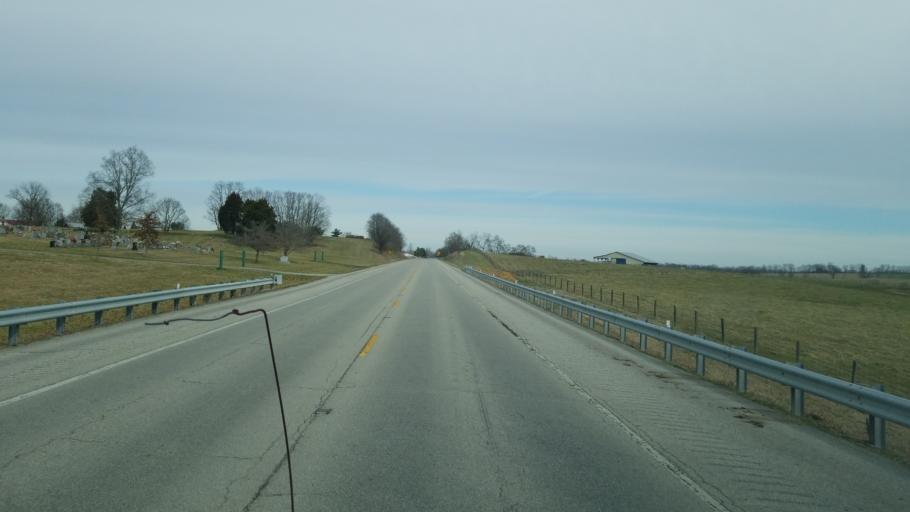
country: US
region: Kentucky
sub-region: Fleming County
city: Flemingsburg
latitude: 38.5126
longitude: -83.8427
